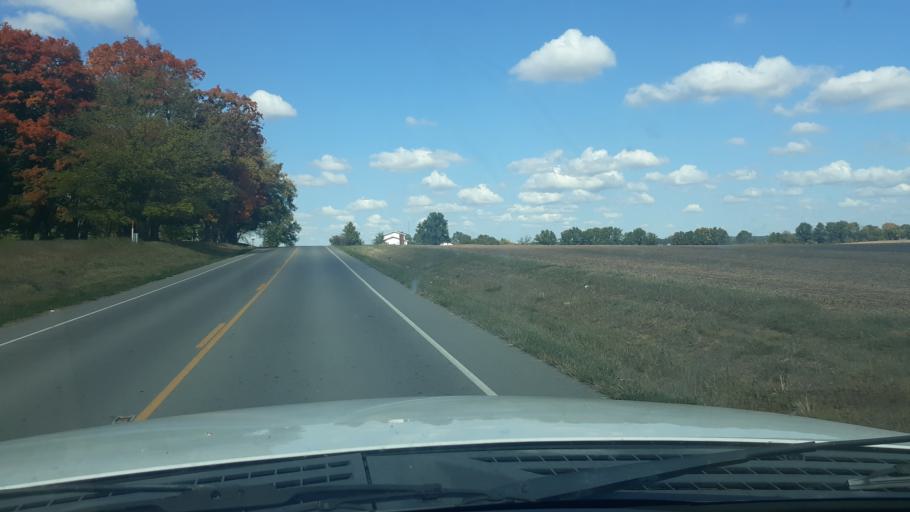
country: US
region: Illinois
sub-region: Saline County
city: Eldorado
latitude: 37.7922
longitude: -88.4847
